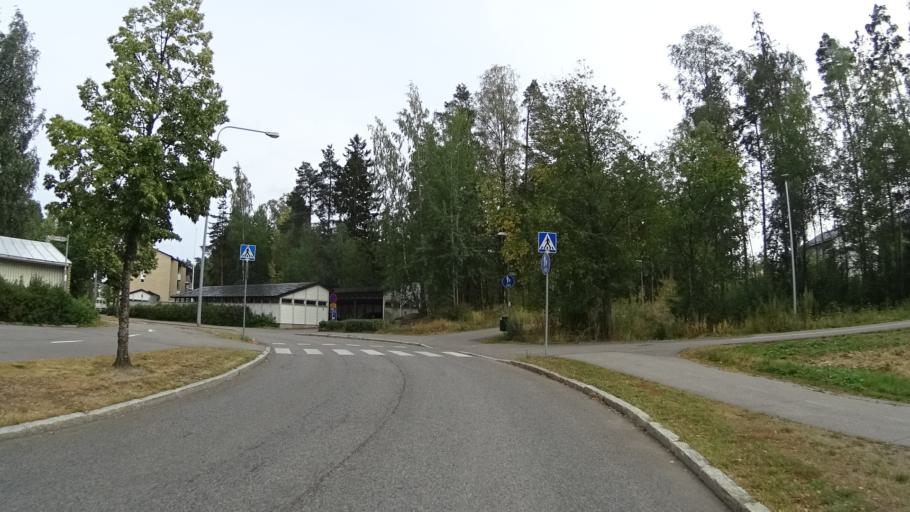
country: FI
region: Uusimaa
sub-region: Helsinki
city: Vantaa
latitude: 60.2325
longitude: 25.0626
